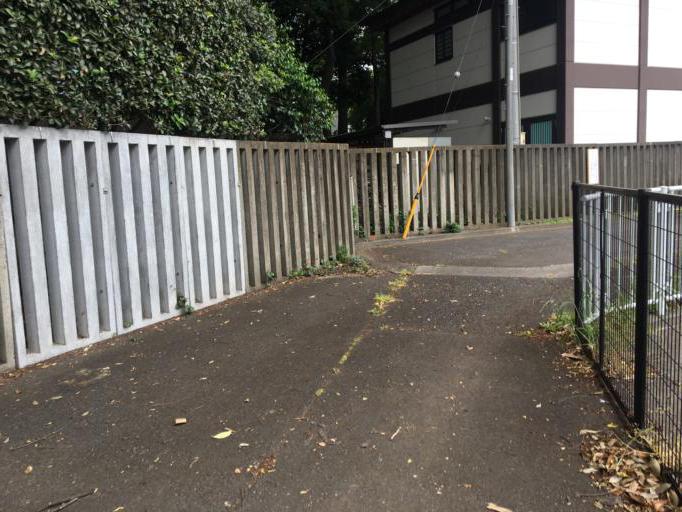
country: JP
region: Tokyo
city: Kokubunji
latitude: 35.6671
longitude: 139.4797
